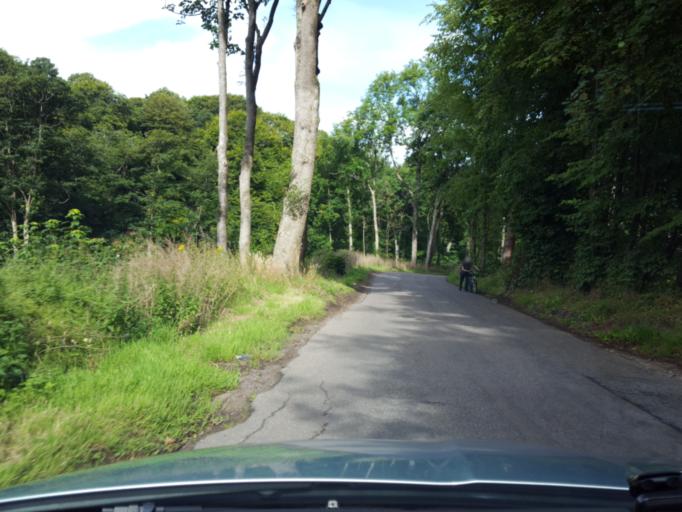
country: GB
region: Scotland
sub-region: Moray
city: Rothes
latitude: 57.4777
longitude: -3.1988
